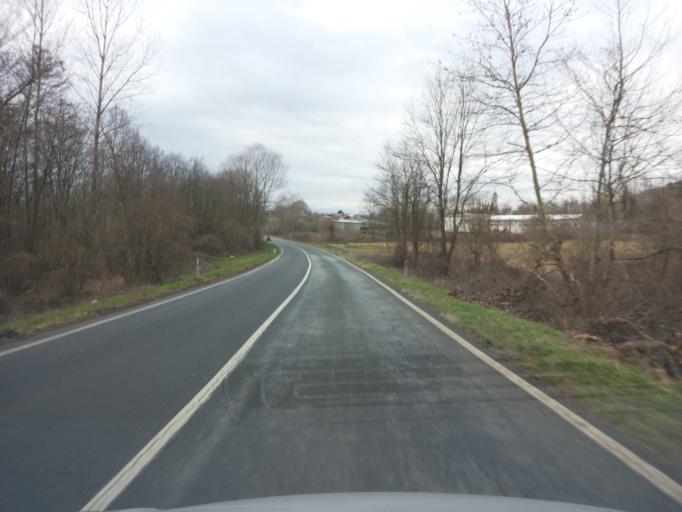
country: IT
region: Piedmont
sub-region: Provincia di Torino
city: Vestigne
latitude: 45.3825
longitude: 7.9615
